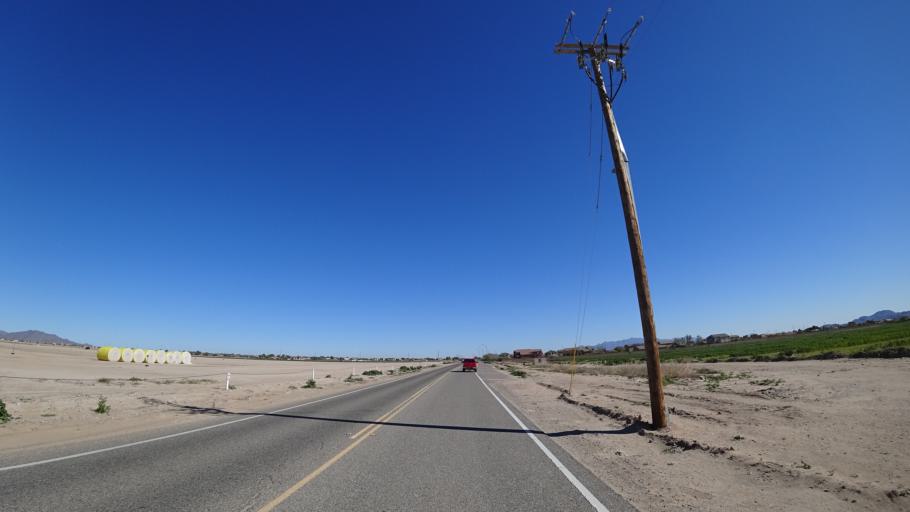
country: US
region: Arizona
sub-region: Maricopa County
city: Buckeye
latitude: 33.3919
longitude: -112.5981
